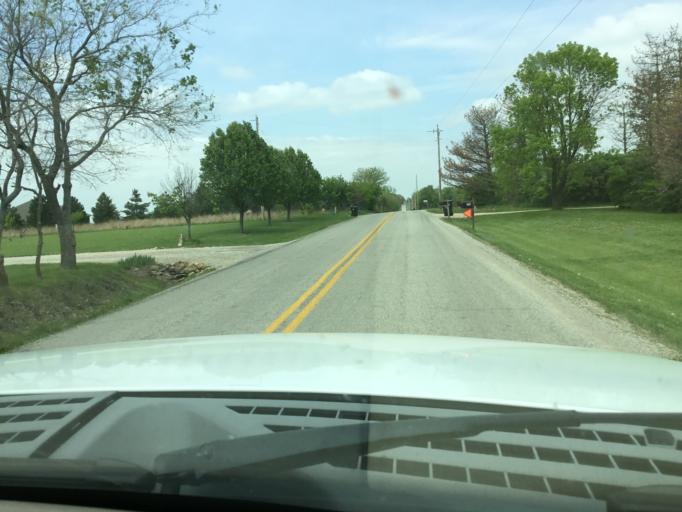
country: US
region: Kansas
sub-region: Shawnee County
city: Topeka
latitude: 38.9645
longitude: -95.6142
